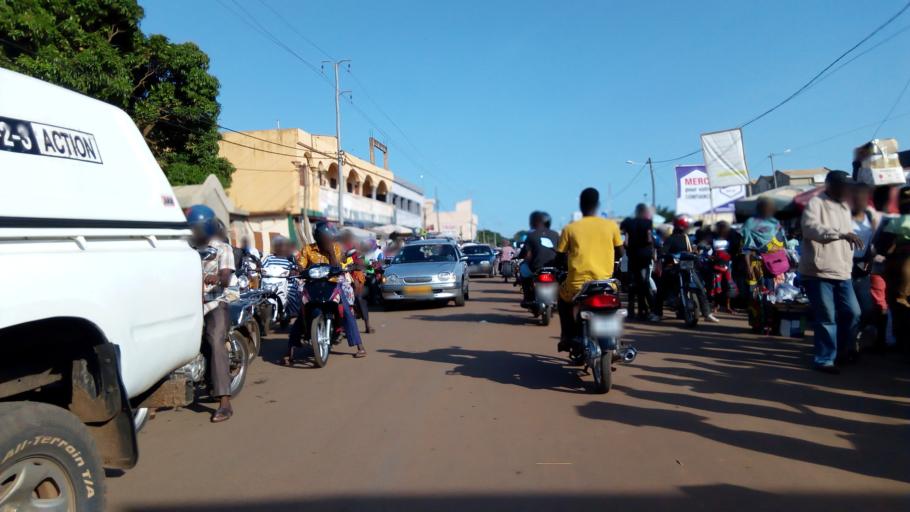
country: TG
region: Maritime
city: Lome
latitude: 6.2322
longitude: 1.1978
